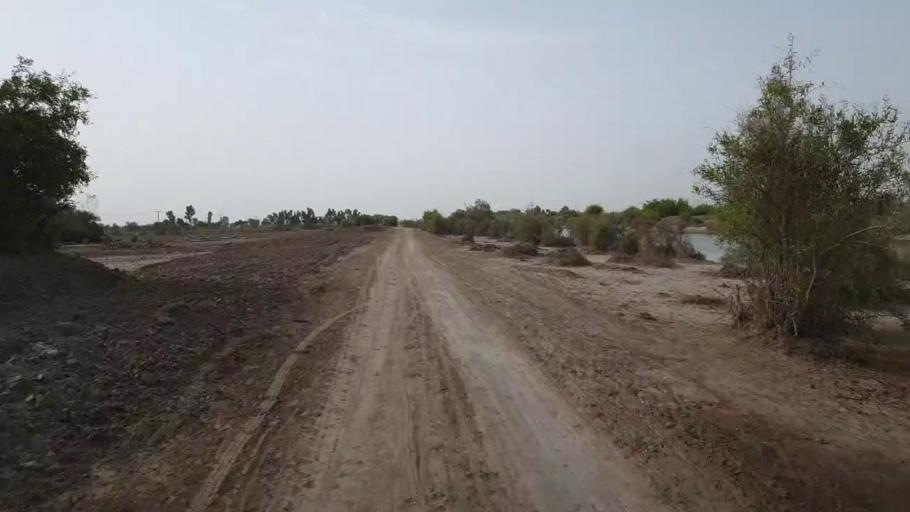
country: PK
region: Sindh
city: Daur
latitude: 26.4206
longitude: 68.1594
